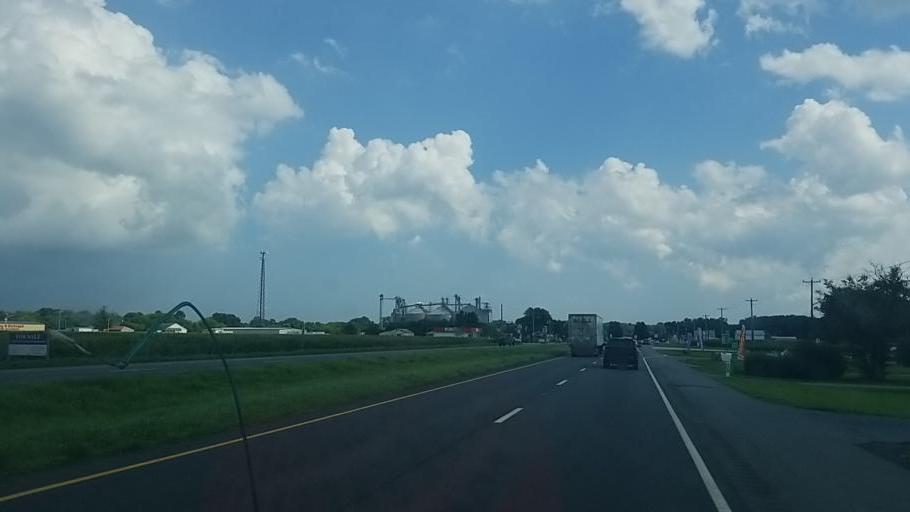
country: US
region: Delaware
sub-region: Sussex County
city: Selbyville
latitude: 38.5226
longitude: -75.2438
